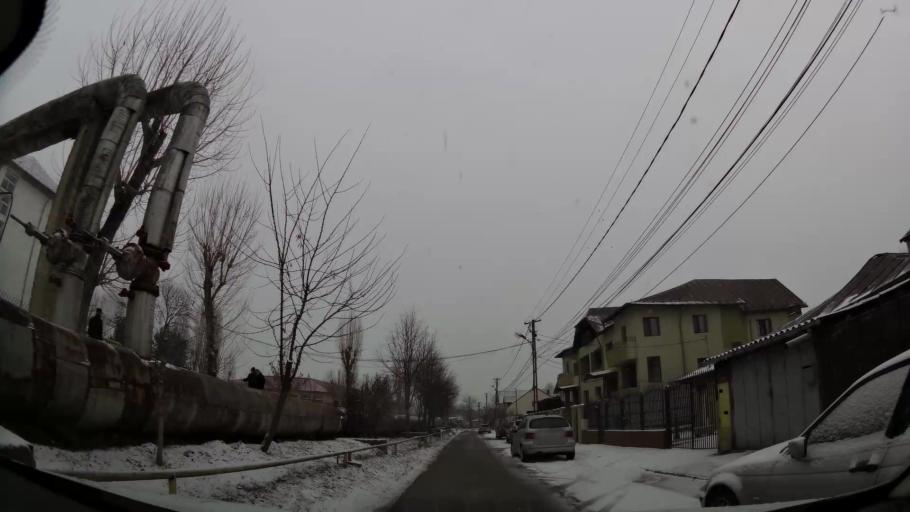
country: RO
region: Dambovita
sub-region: Municipiul Targoviste
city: Targoviste
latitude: 44.9287
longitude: 25.4472
